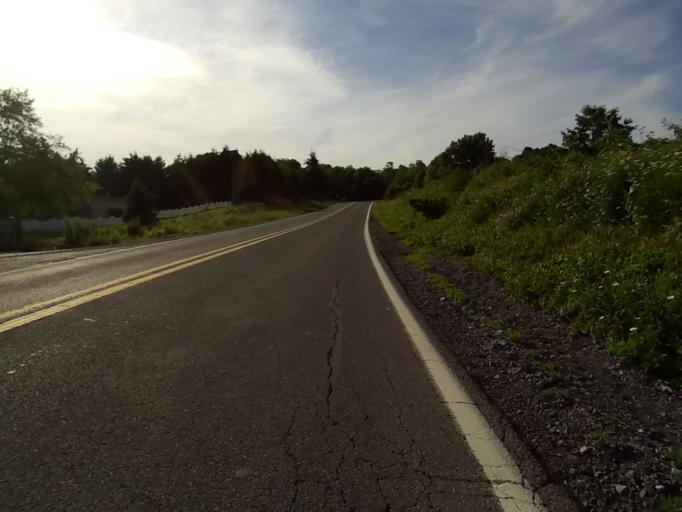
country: US
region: Pennsylvania
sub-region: Centre County
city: Park Forest Village
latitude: 40.8141
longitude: -77.9574
